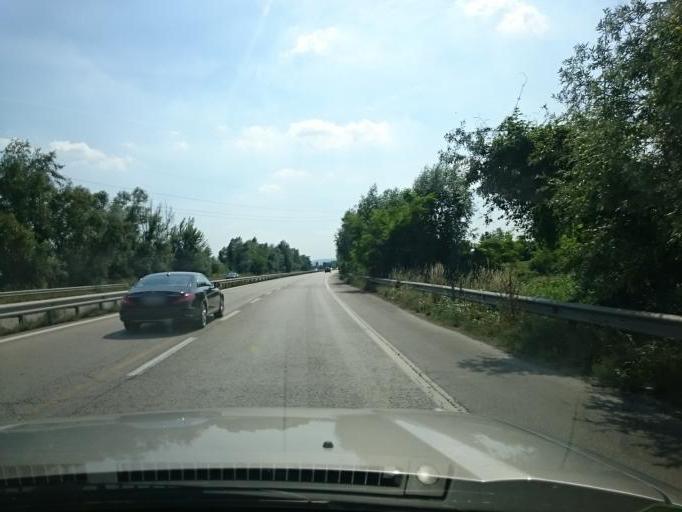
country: IT
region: Veneto
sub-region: Provincia di Padova
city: Ponte San Nicolo
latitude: 45.3716
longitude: 11.9038
